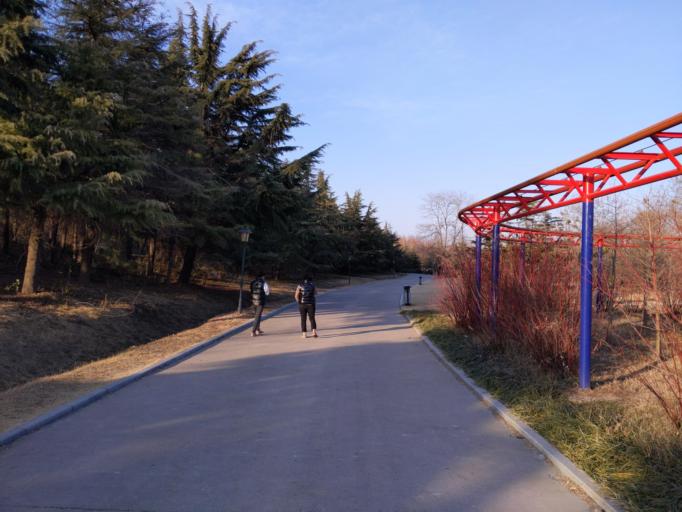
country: CN
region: Henan Sheng
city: Puyang
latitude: 35.7786
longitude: 114.9506
